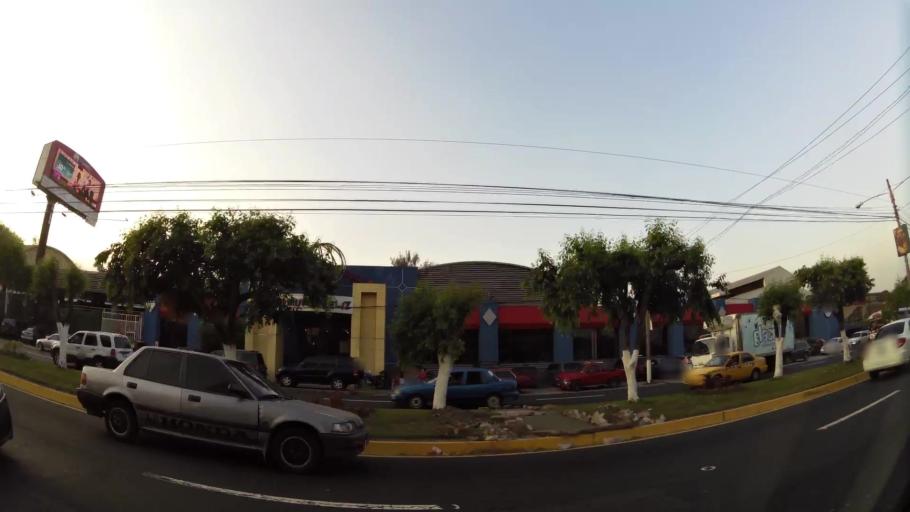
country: SV
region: San Salvador
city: San Salvador
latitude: 13.7084
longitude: -89.2109
